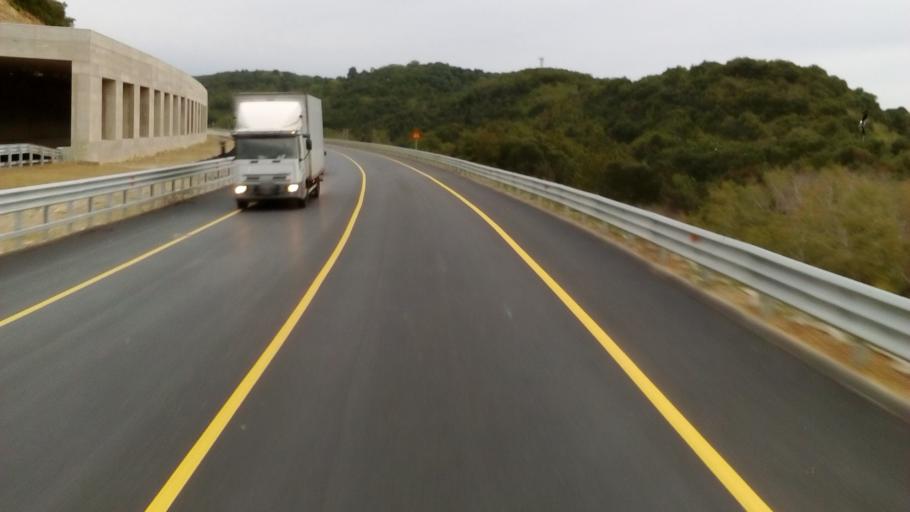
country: IT
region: Tuscany
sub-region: Provincia di Grosseto
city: Civitella Marittima
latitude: 43.0425
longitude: 11.2852
